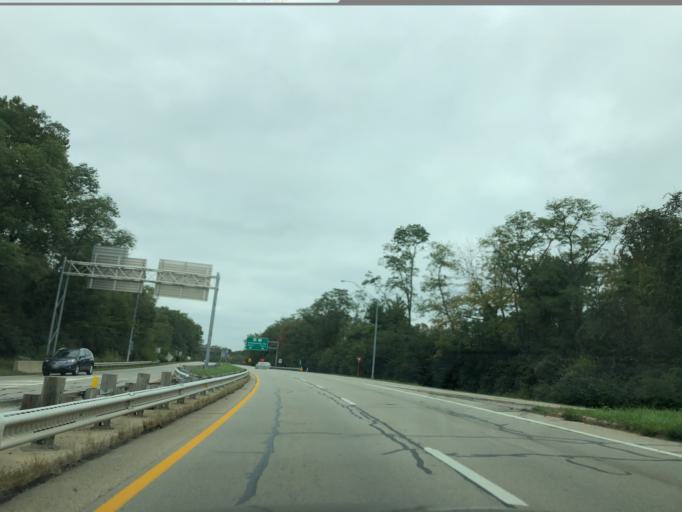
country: US
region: Ohio
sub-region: Hamilton County
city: Montgomery
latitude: 39.2239
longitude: -84.3640
